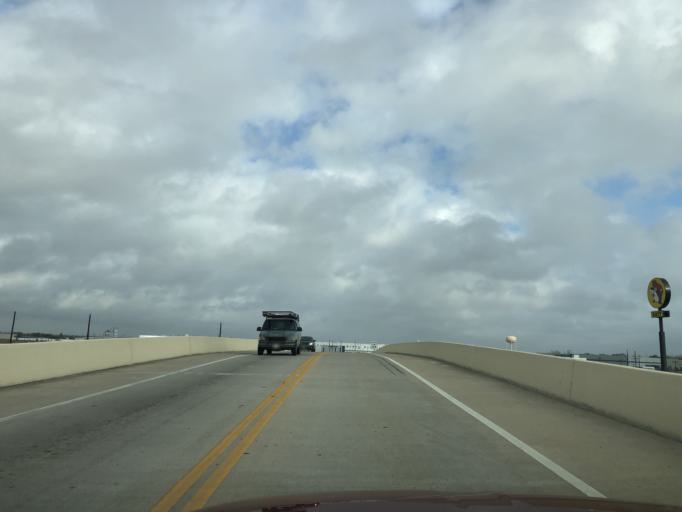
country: US
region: Texas
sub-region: Harris County
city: Katy
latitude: 29.7765
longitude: -95.8502
